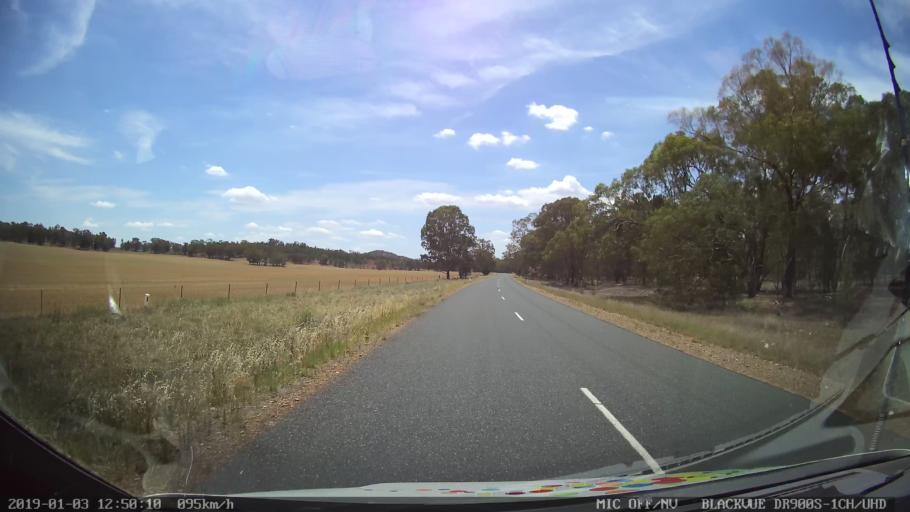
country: AU
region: New South Wales
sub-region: Weddin
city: Grenfell
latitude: -33.6943
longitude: 148.2672
